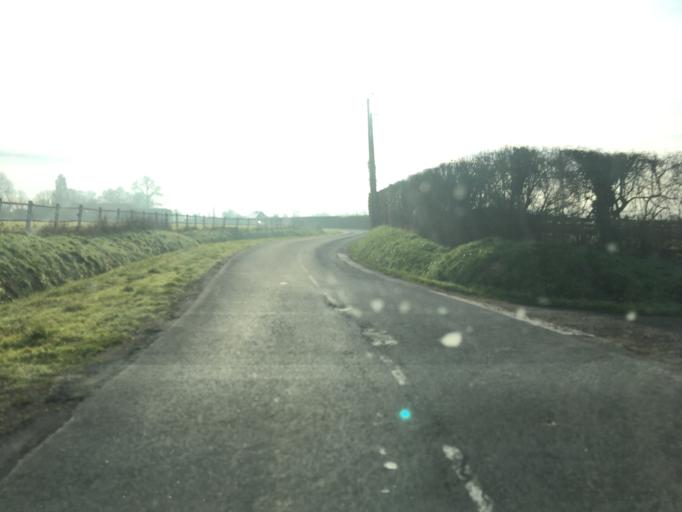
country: FR
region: Lower Normandy
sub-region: Departement du Calvados
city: Dozule
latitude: 49.2091
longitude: -0.0686
